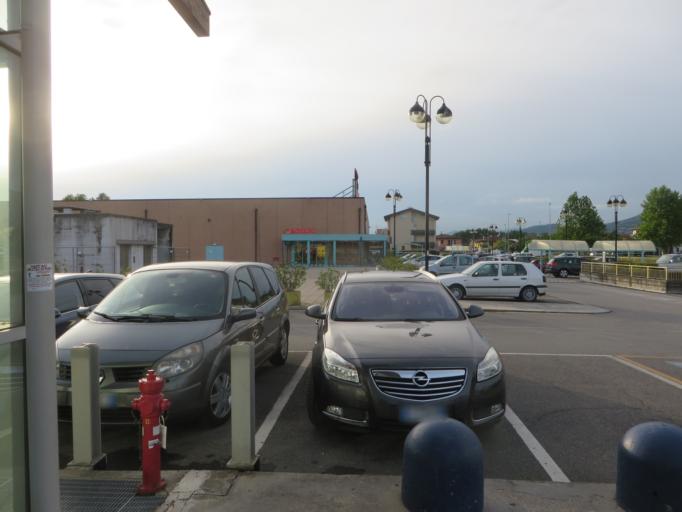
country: IT
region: Lombardy
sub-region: Provincia di Brescia
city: Buffalora-Bettole
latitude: 45.4913
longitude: 10.2737
